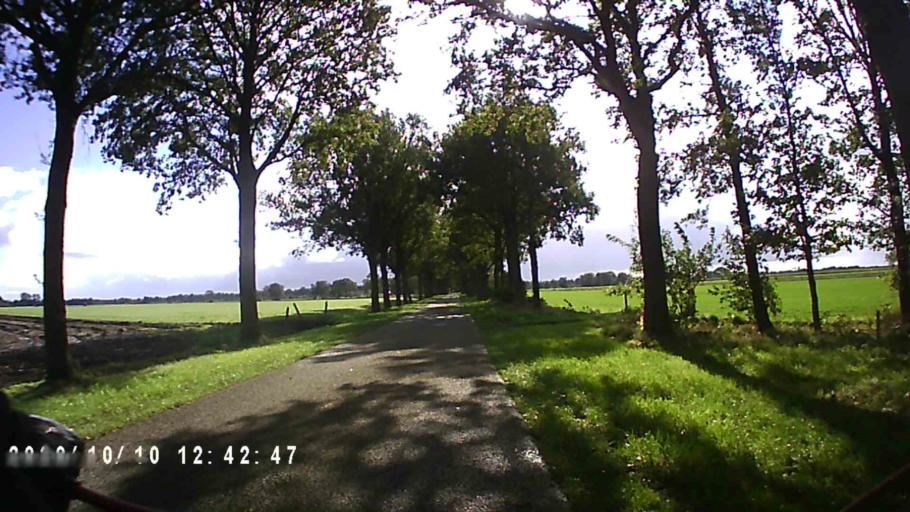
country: NL
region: Friesland
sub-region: Gemeente Weststellingwerf
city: Noordwolde
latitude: 52.9340
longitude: 6.2199
